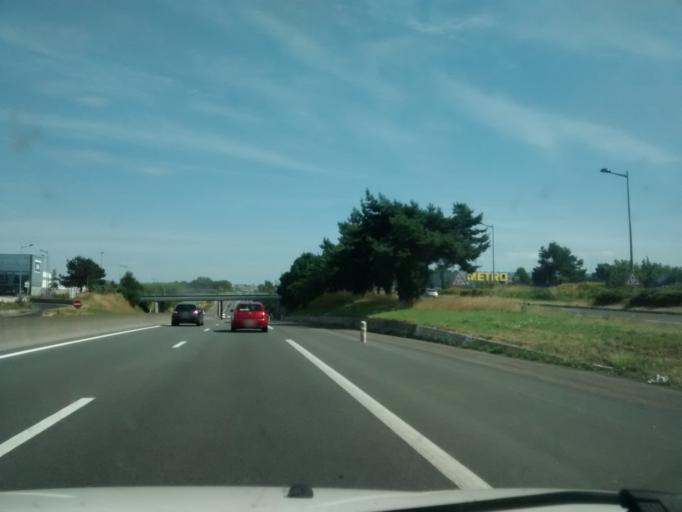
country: FR
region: Brittany
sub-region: Departement des Cotes-d'Armor
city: Langueux
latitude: 48.5065
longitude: -2.7350
